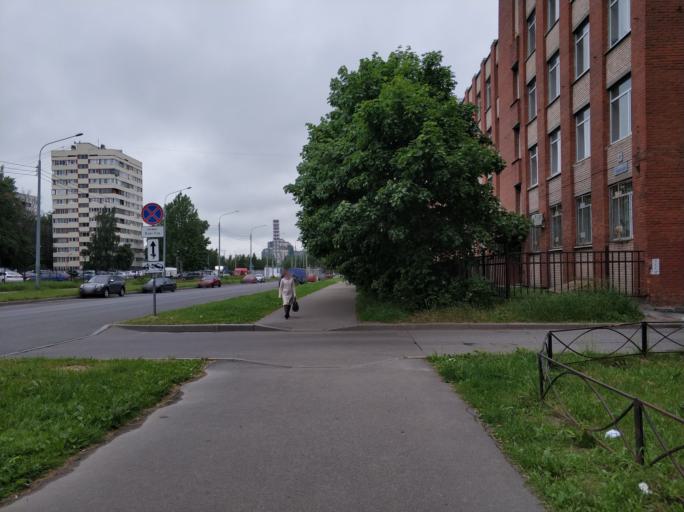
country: RU
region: St.-Petersburg
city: Grazhdanka
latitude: 60.0432
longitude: 30.4165
